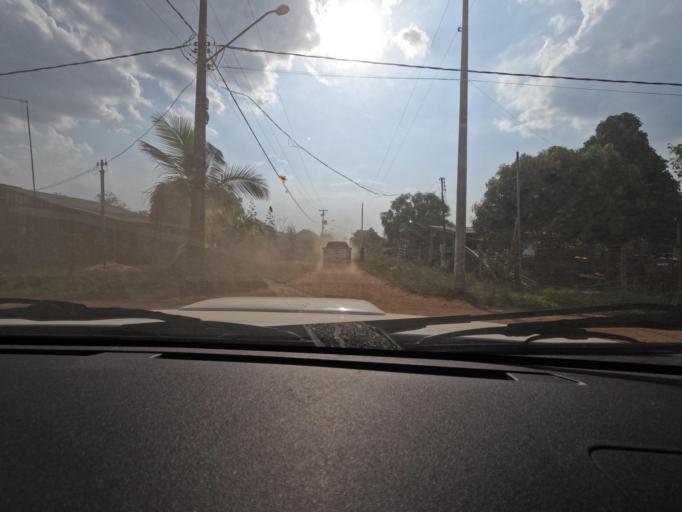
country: BR
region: Rondonia
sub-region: Porto Velho
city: Porto Velho
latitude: -8.5753
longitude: -63.9938
